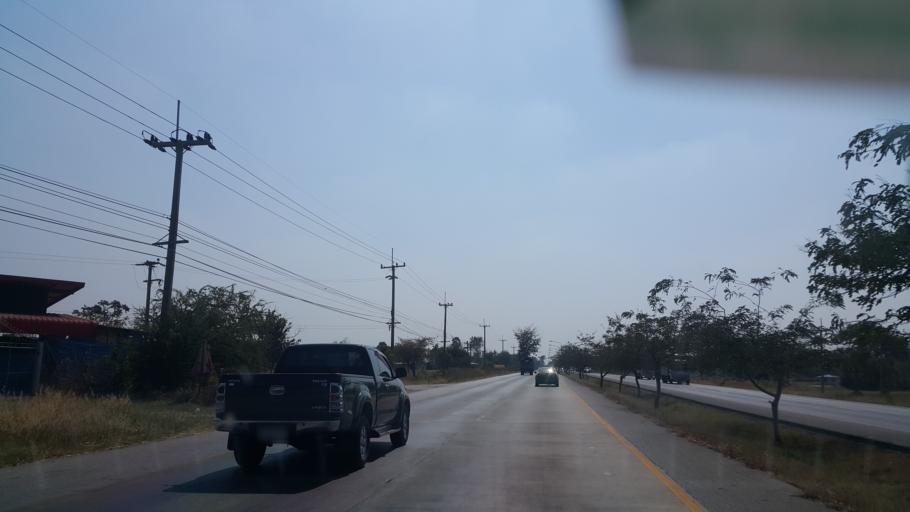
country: TH
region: Nakhon Ratchasima
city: Non Daeng
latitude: 15.4182
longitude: 102.4821
